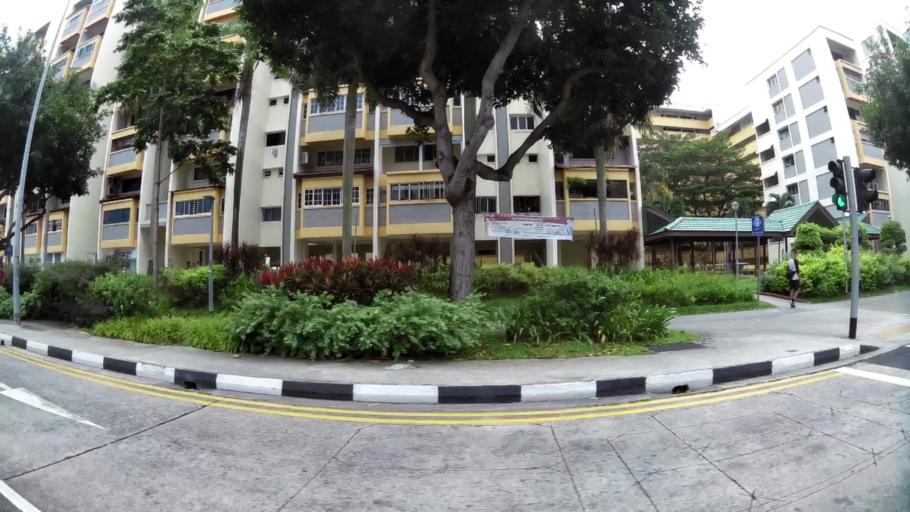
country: SG
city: Singapore
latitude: 1.3516
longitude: 103.9434
